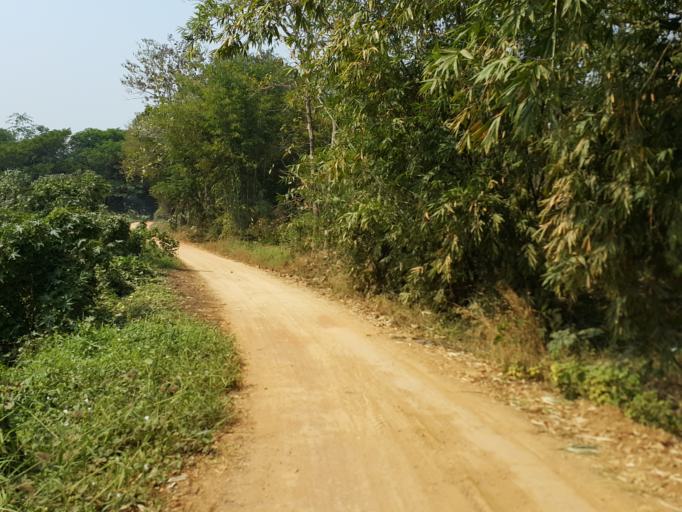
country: TH
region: Sukhothai
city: Thung Saliam
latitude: 17.3222
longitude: 99.5134
